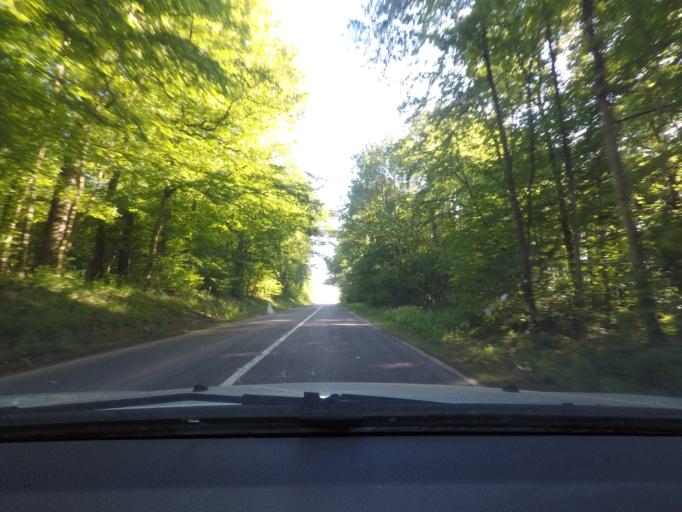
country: BE
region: Wallonia
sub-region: Province de Namur
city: Rochefort
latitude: 50.2102
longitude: 5.1471
